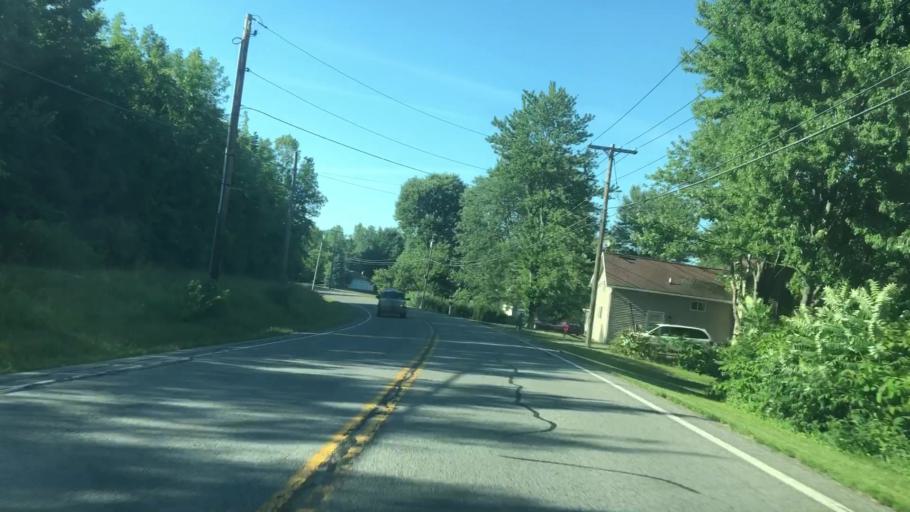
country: US
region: New York
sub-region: Wayne County
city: Ontario
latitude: 43.1785
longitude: -77.2857
